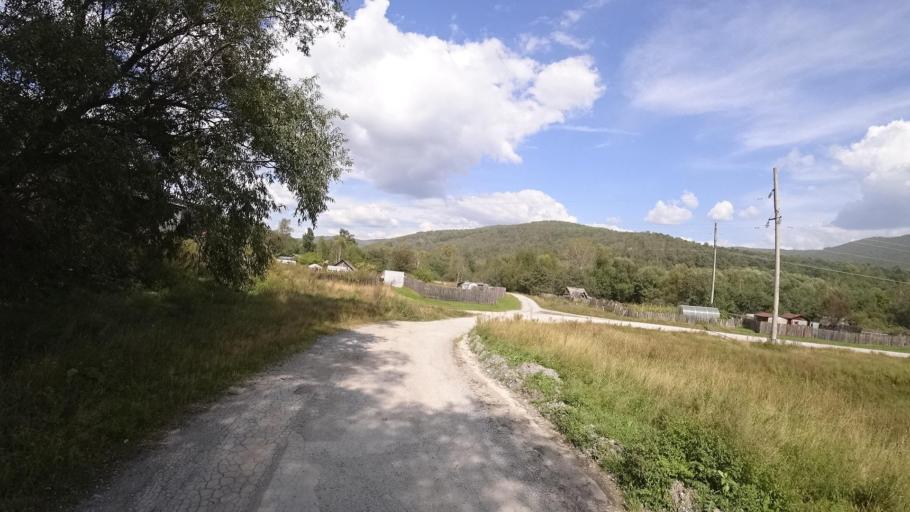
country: RU
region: Jewish Autonomous Oblast
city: Londoko
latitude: 49.0278
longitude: 131.9244
